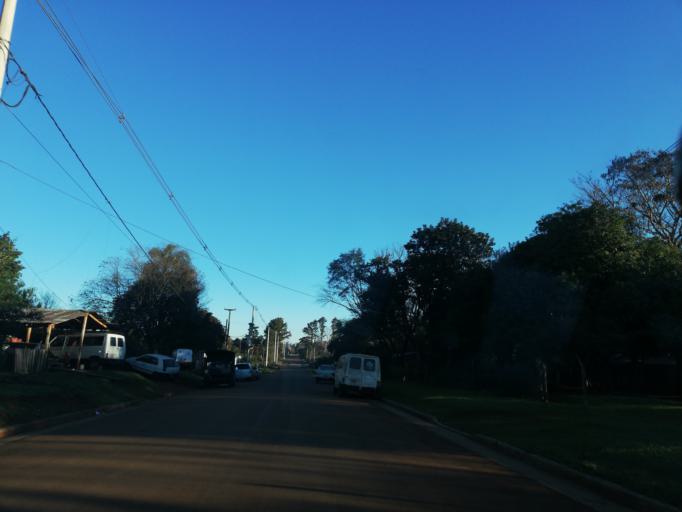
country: AR
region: Misiones
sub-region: Departamento de Candelaria
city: Candelaria
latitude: -27.4628
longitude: -55.7488
